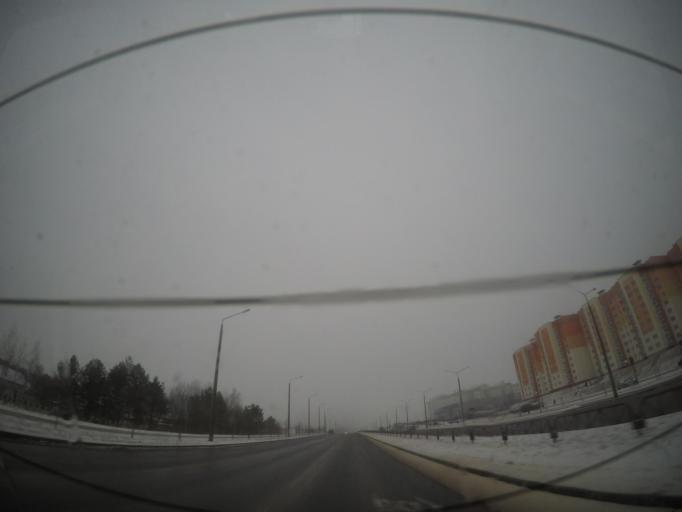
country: BY
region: Grodnenskaya
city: Hrodna
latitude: 53.6172
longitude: 23.8218
